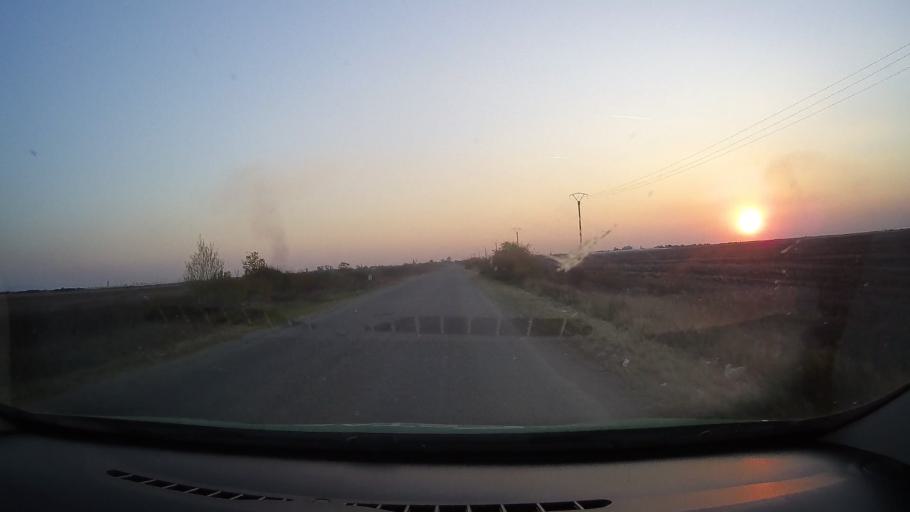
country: RO
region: Arad
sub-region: Comuna Olari
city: Olari
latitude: 46.3982
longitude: 21.5624
